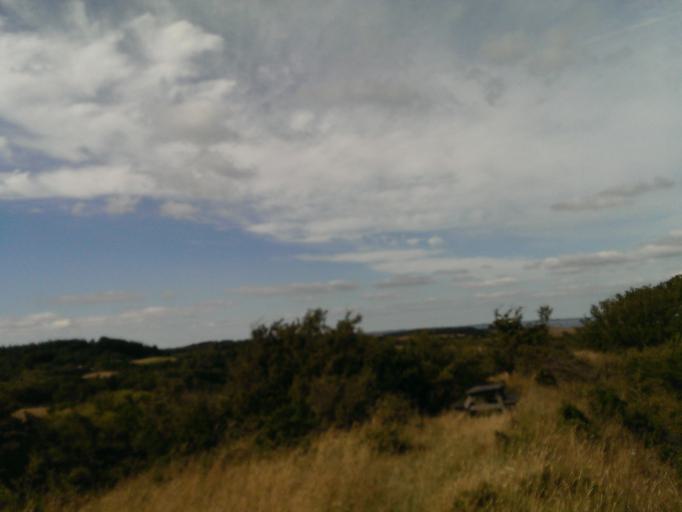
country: DK
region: Central Jutland
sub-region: Syddjurs Kommune
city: Ebeltoft
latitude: 56.1039
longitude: 10.5422
